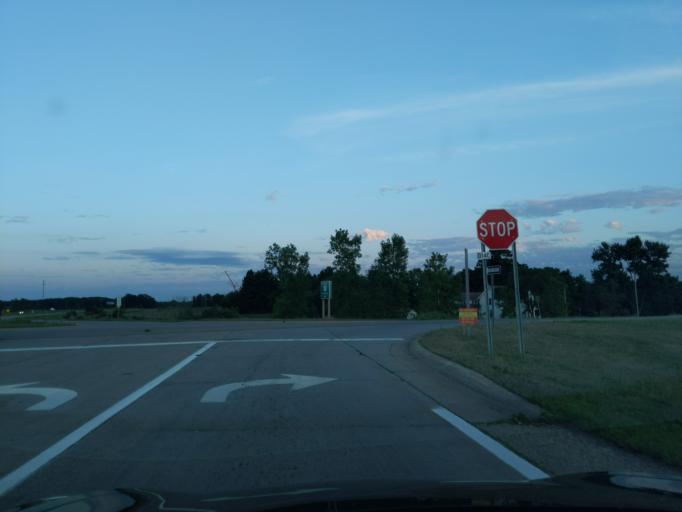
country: US
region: Michigan
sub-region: Clinton County
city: Saint Johns
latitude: 43.0274
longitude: -84.5632
